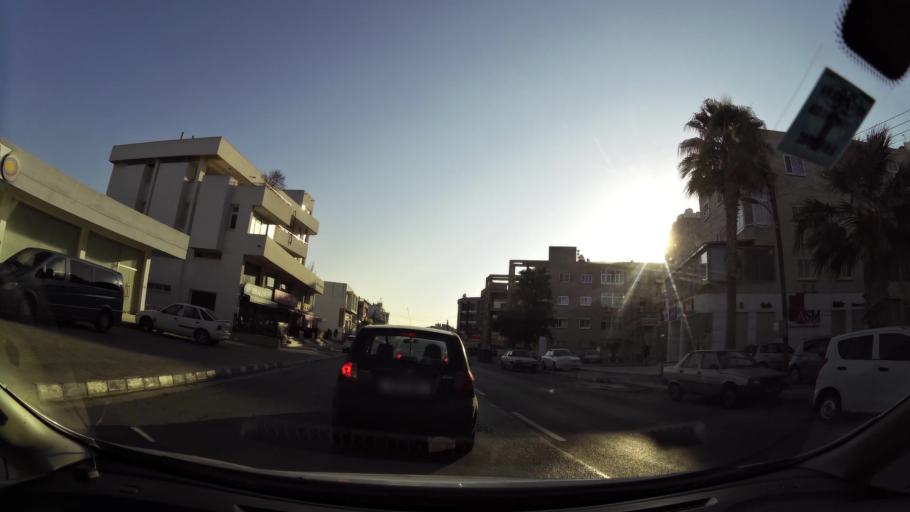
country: CY
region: Lefkosia
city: Nicosia
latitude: 35.1993
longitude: 33.3361
